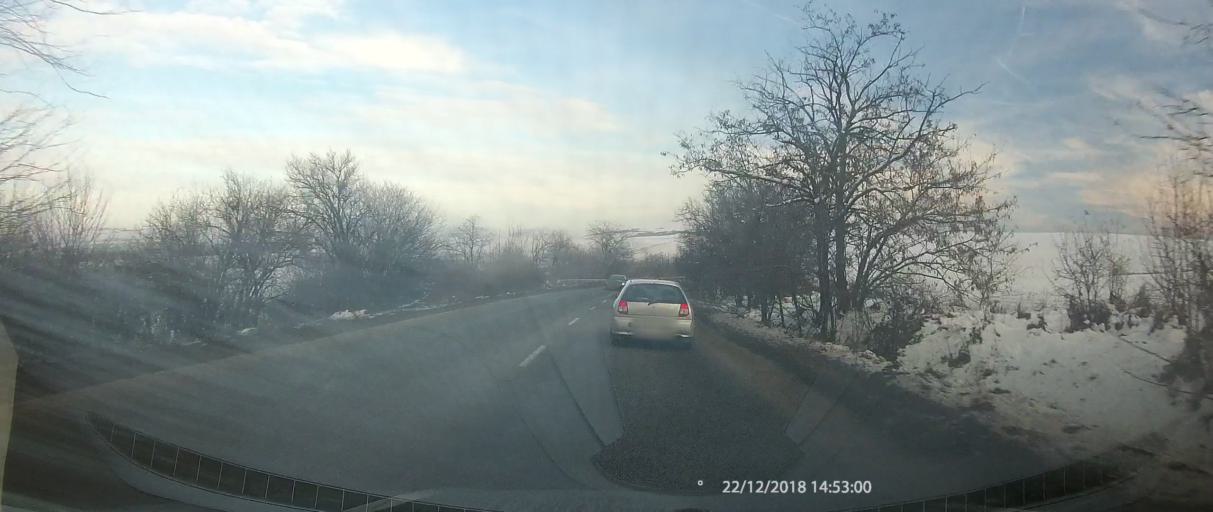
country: BG
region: Veliko Turnovo
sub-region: Obshtina Polski Trumbesh
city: Polski Trumbesh
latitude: 43.4304
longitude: 25.5212
